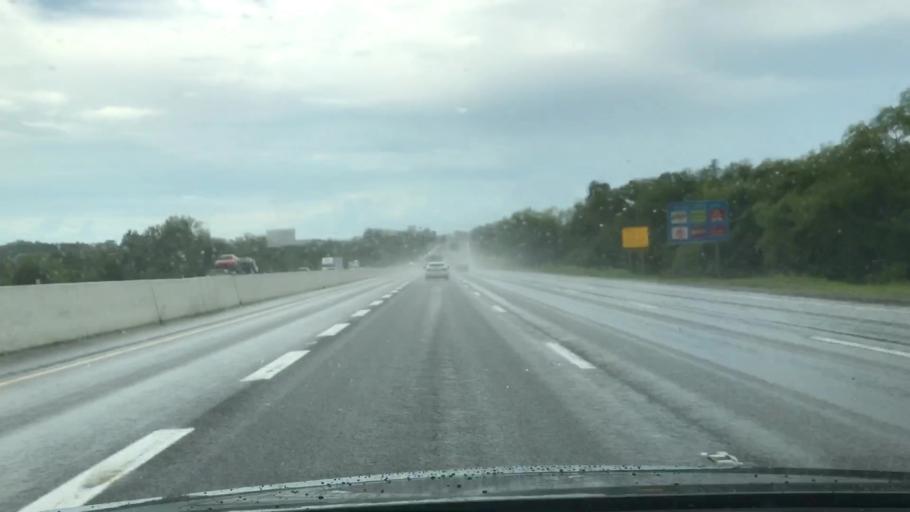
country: US
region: Tennessee
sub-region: Wilson County
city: Mount Juliet
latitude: 36.1740
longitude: -86.4845
